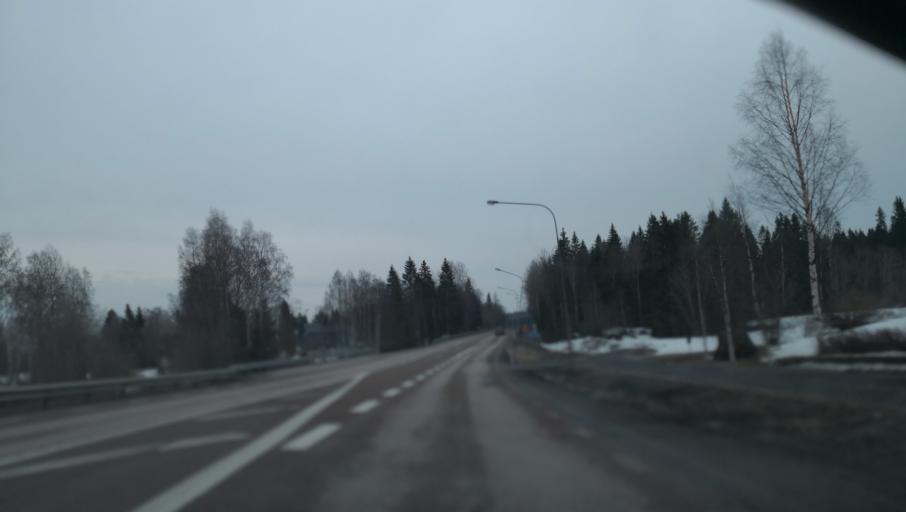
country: SE
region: Vaesternorrland
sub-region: Haernoesands Kommun
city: Haernoesand
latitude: 62.6634
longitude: 17.8541
